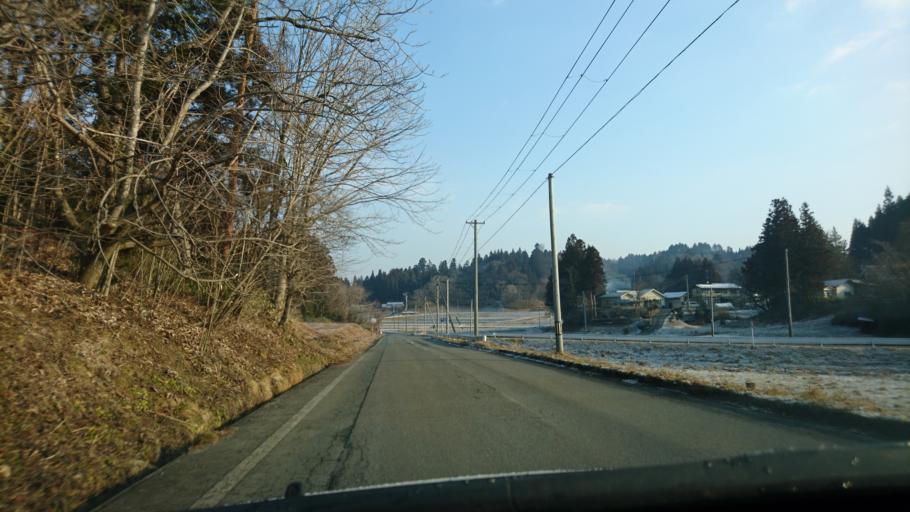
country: JP
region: Iwate
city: Ichinoseki
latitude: 38.9252
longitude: 141.3859
